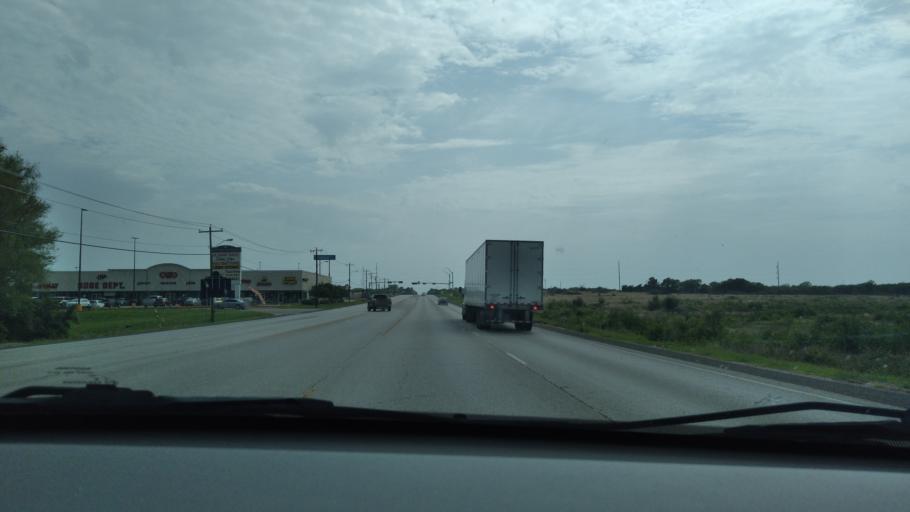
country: US
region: Texas
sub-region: Navarro County
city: Corsicana
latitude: 32.0695
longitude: -96.5061
